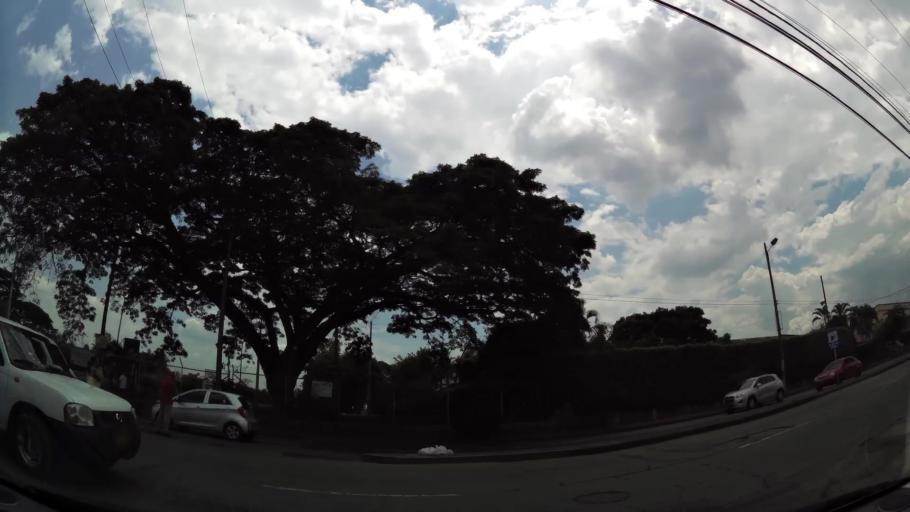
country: CO
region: Valle del Cauca
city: Cali
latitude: 3.4648
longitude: -76.4943
